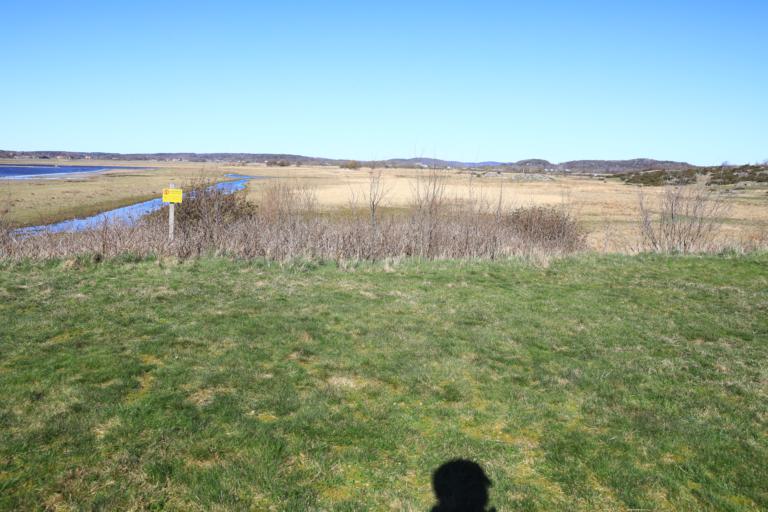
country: SE
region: Halland
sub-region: Varbergs Kommun
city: Varberg
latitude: 57.1279
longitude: 12.2531
